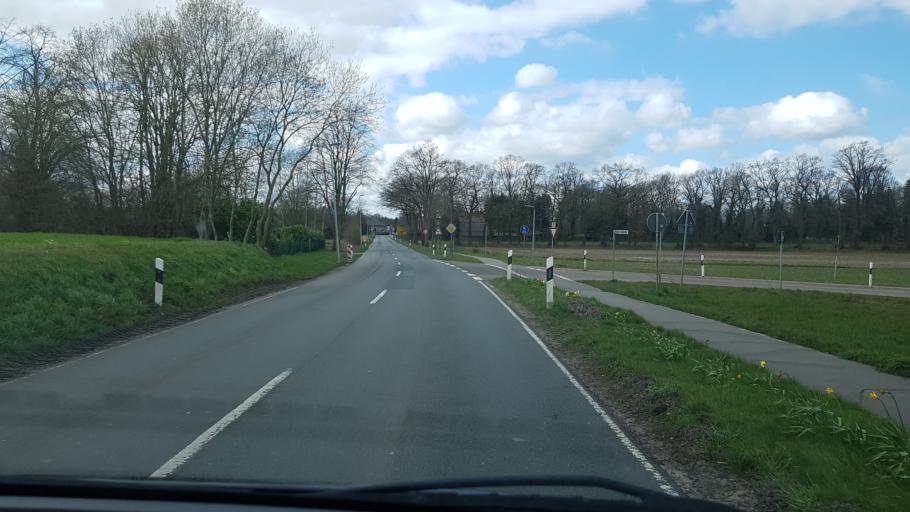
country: DE
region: Lower Saxony
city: Edewecht
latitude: 53.1217
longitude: 7.9356
